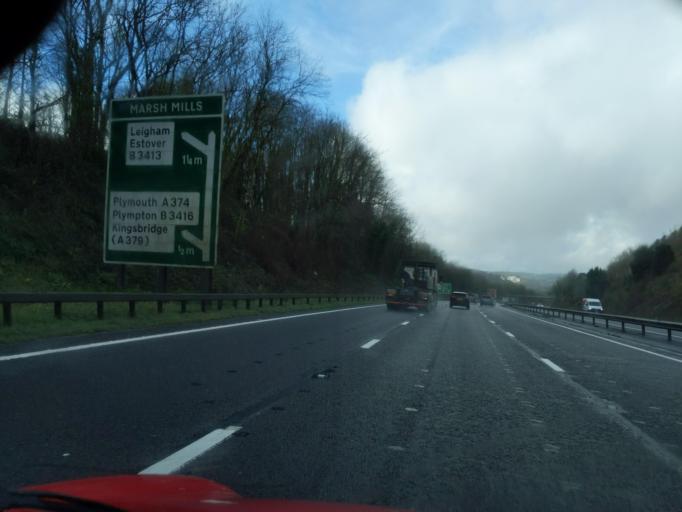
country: GB
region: England
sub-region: Devon
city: Plympton
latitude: 50.3802
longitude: -4.0737
